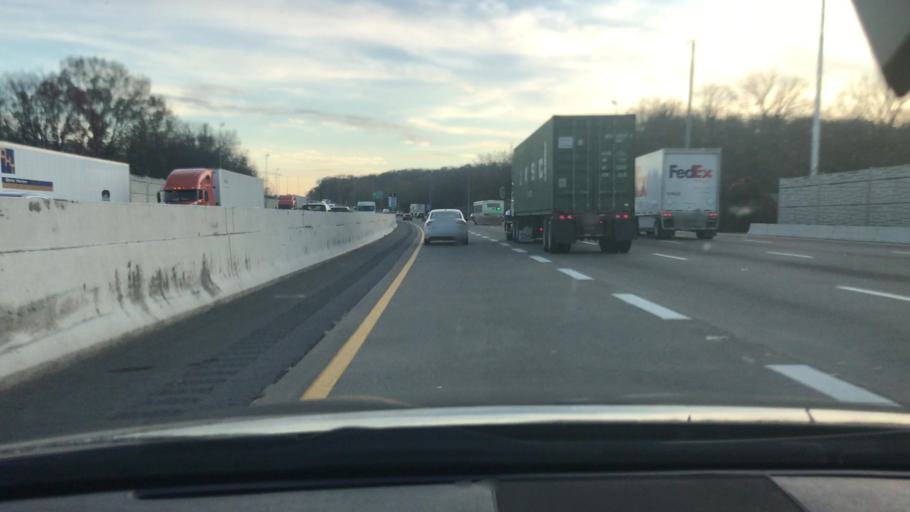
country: US
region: Tennessee
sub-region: Davidson County
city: Goodlettsville
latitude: 36.2788
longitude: -86.7342
